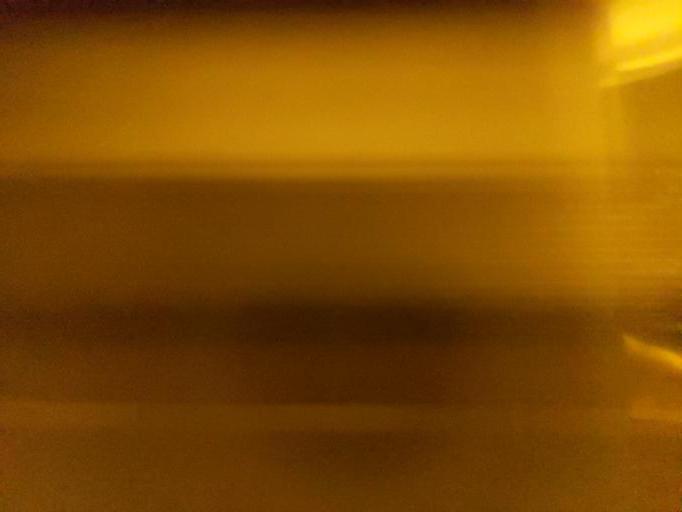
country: JP
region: Miyagi
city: Iwanuma
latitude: 38.1629
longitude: 140.8510
